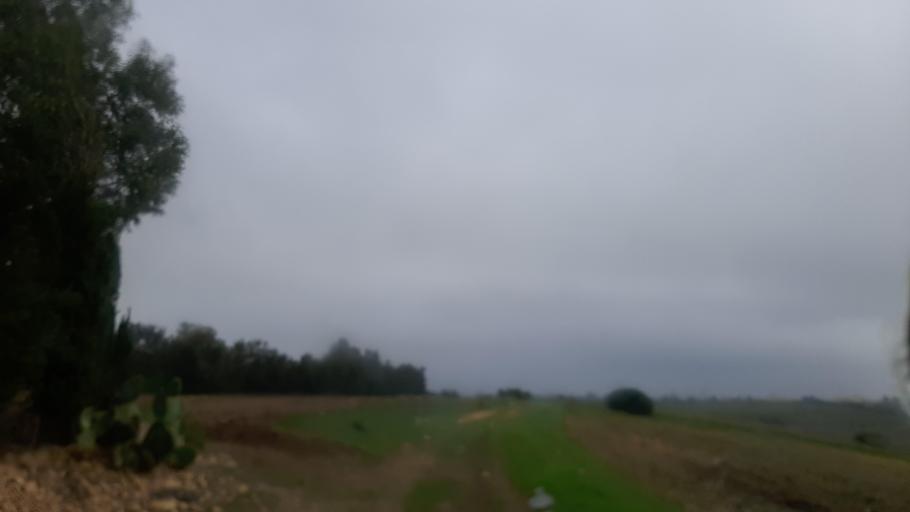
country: TN
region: Nabul
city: Qulaybiyah
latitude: 36.8288
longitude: 11.0333
